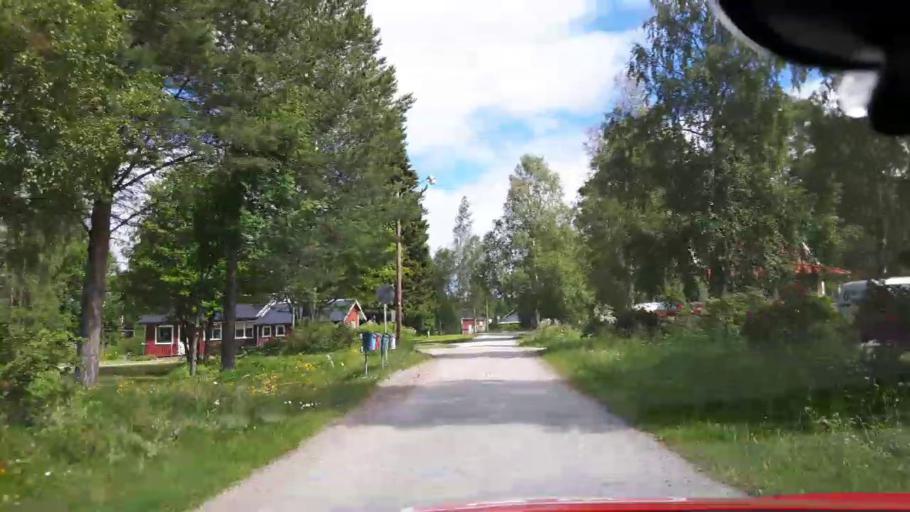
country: SE
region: Jaemtland
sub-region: Braecke Kommun
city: Braecke
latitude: 62.8311
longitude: 15.3089
